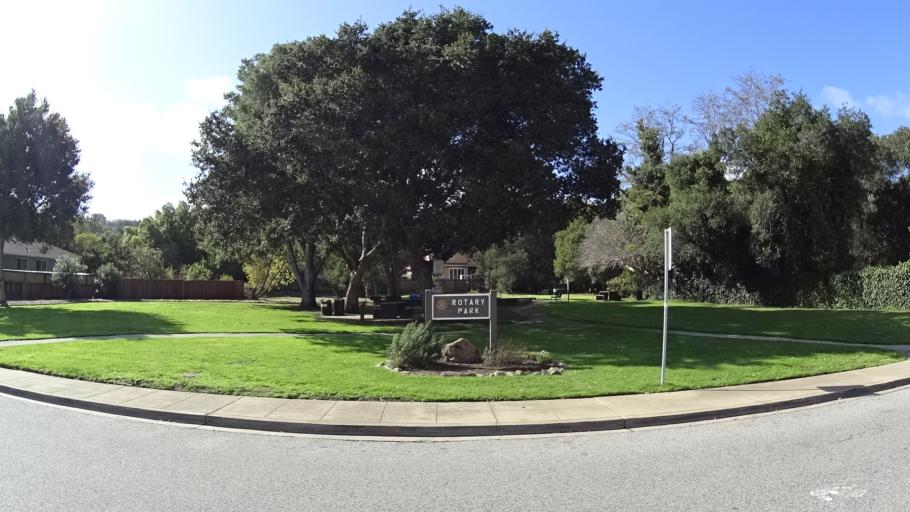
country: US
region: California
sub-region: San Mateo County
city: Millbrae
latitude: 37.5935
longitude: -122.3960
